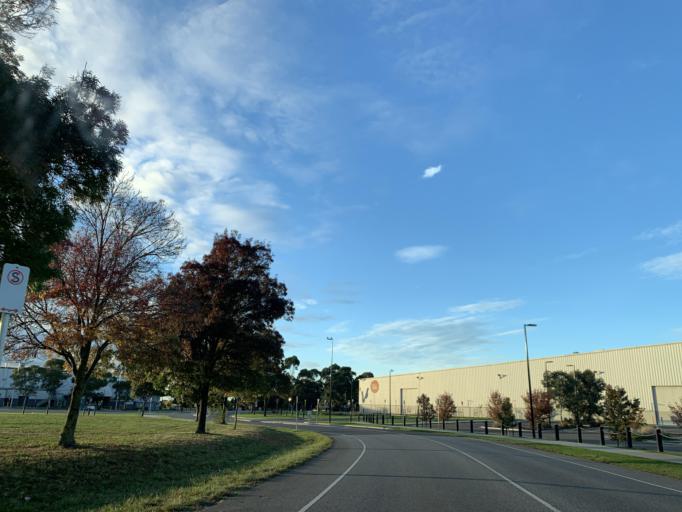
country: AU
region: Victoria
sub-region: Casey
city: Cranbourne East
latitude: -38.1116
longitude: 145.2957
